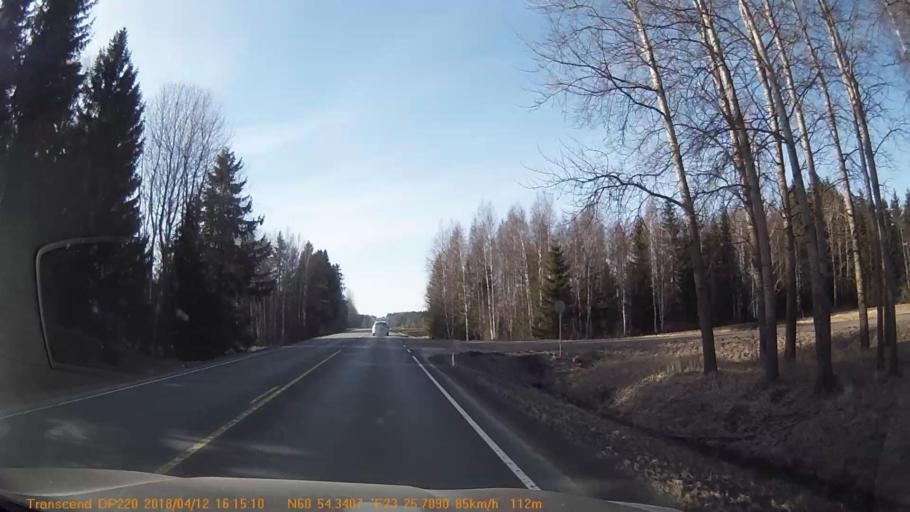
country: FI
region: Haeme
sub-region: Forssa
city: Humppila
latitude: 60.9058
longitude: 23.4283
